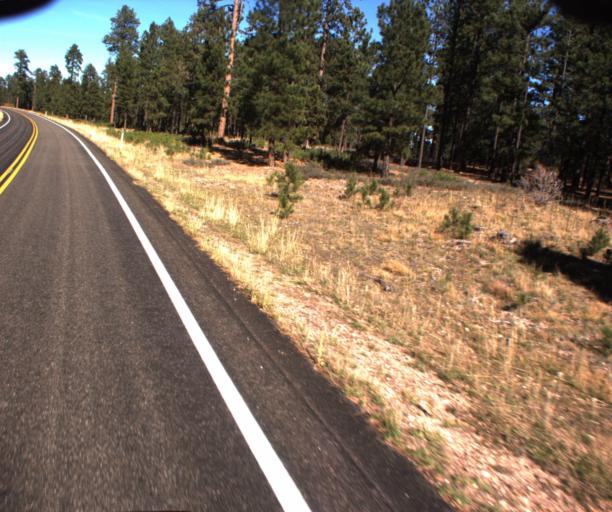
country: US
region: Arizona
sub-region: Coconino County
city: Fredonia
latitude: 36.6928
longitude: -112.2147
